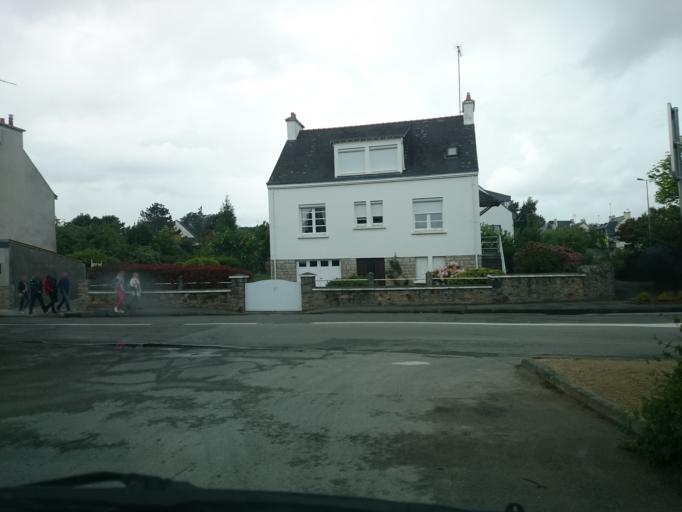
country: FR
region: Brittany
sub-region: Departement du Morbihan
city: Vannes
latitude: 47.6383
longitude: -2.7679
